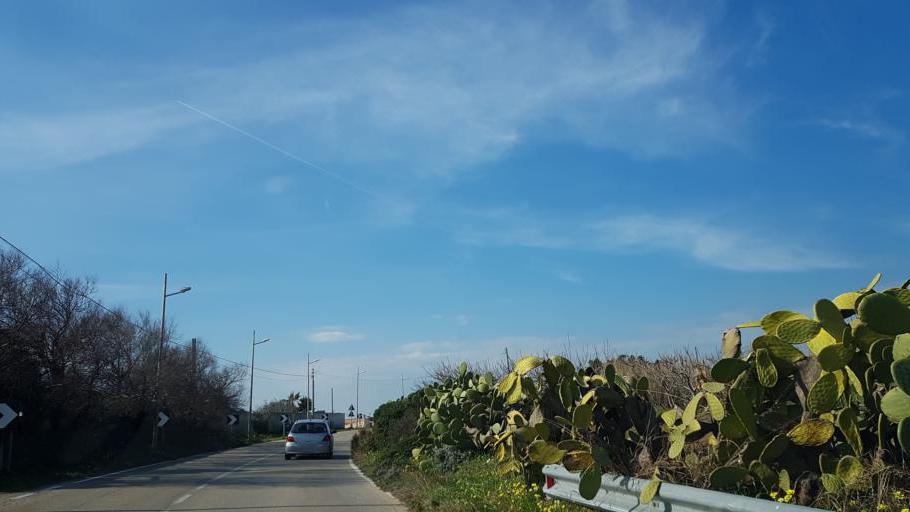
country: IT
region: Apulia
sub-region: Provincia di Brindisi
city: Brindisi
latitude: 40.6846
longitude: 17.8738
